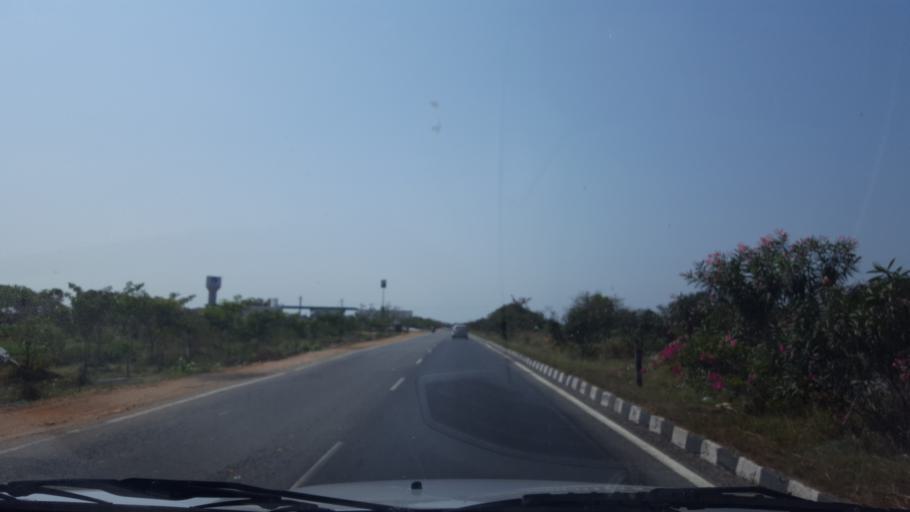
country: IN
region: Andhra Pradesh
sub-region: Guntur
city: Chilakalurupet
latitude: 16.0746
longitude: 80.1555
